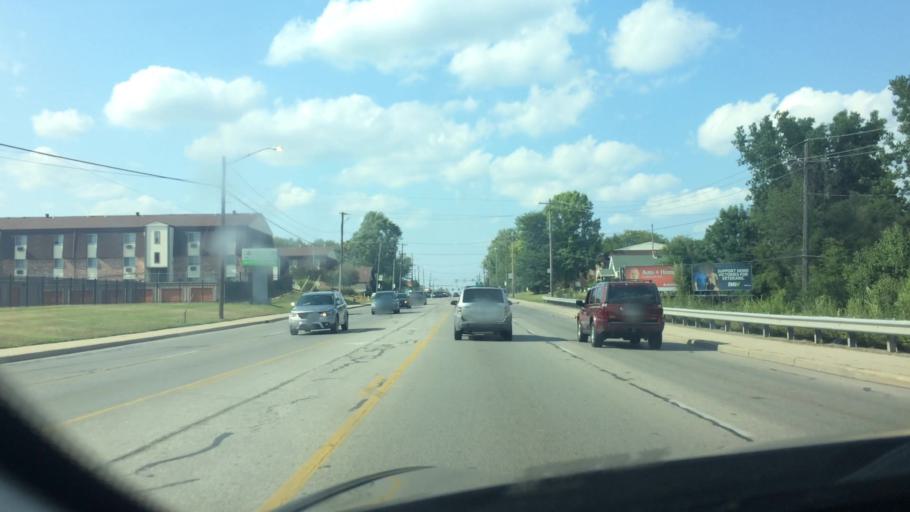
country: US
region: Ohio
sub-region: Lucas County
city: Ottawa Hills
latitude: 41.6202
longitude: -83.6257
